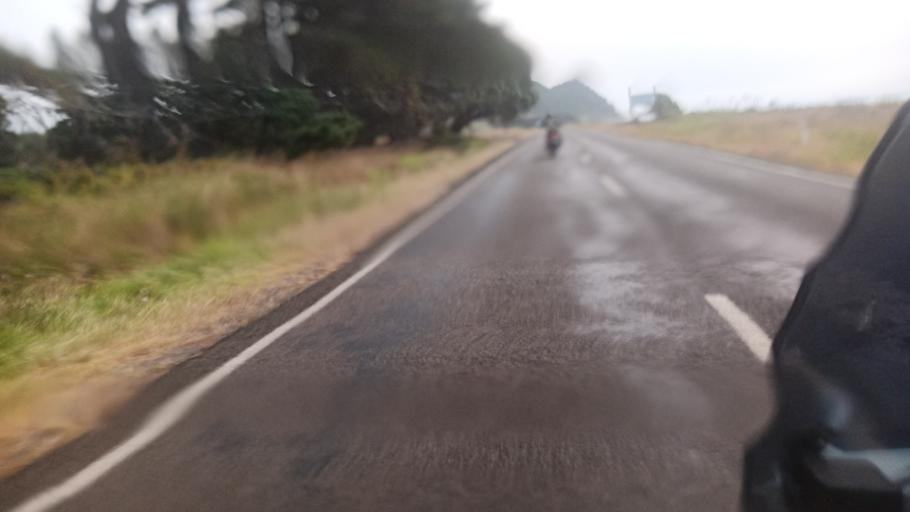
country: NZ
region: Bay of Plenty
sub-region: Opotiki District
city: Opotiki
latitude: -37.9264
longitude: 177.5169
